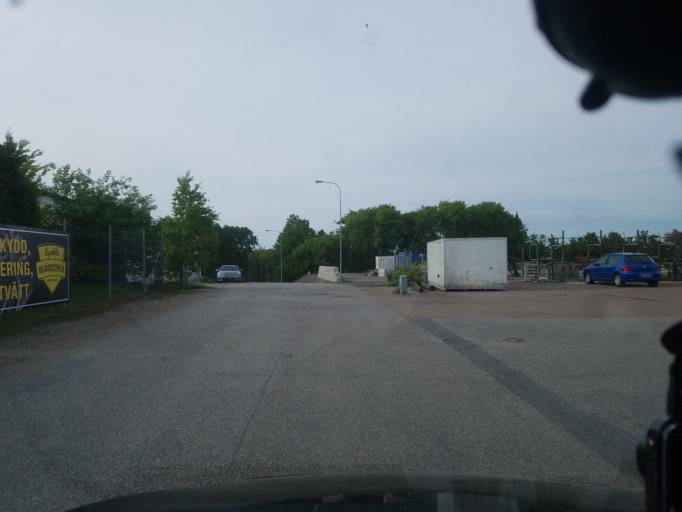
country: SE
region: Vaestra Goetaland
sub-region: Lysekils Kommun
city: Lysekil
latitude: 58.2882
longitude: 11.4570
